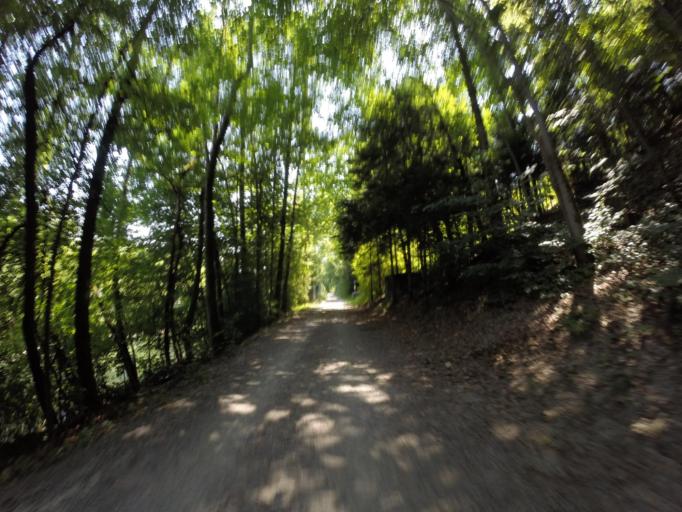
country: CH
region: Bern
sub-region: Bern-Mittelland District
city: Kehrsatz
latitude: 46.9250
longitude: 7.4706
